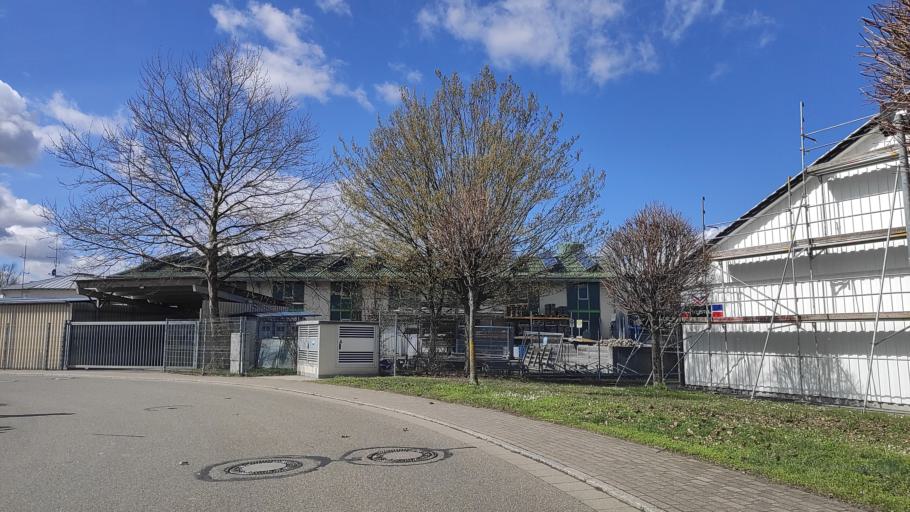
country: DE
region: Baden-Wuerttemberg
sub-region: Freiburg Region
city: Bad Krozingen
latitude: 47.9245
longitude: 7.7023
